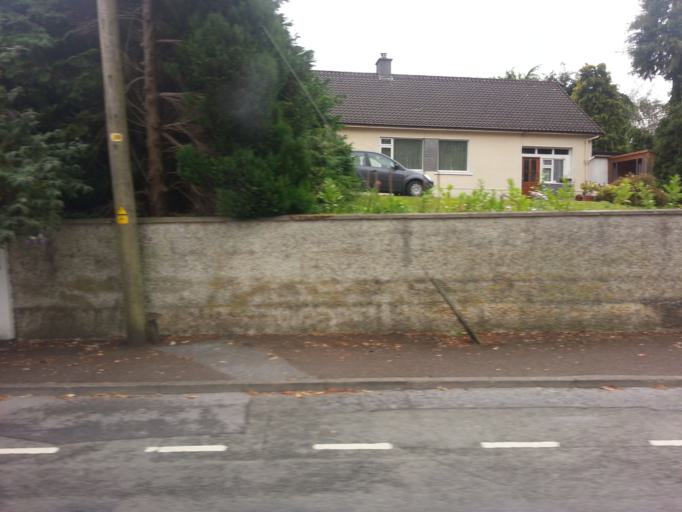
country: IE
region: Leinster
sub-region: Kilkenny
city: Kilkenny
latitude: 52.6461
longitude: -7.2409
